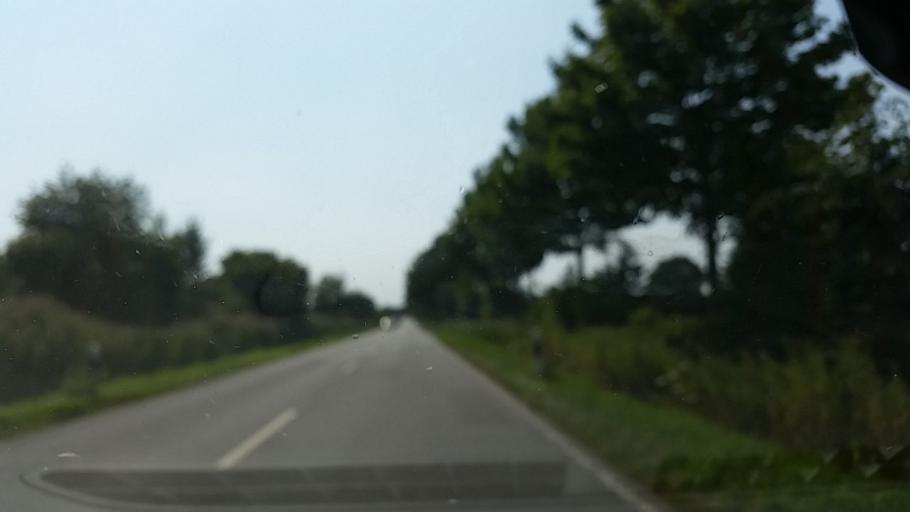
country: DE
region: Schleswig-Holstein
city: Muhlenrade
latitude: 53.6006
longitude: 10.4984
